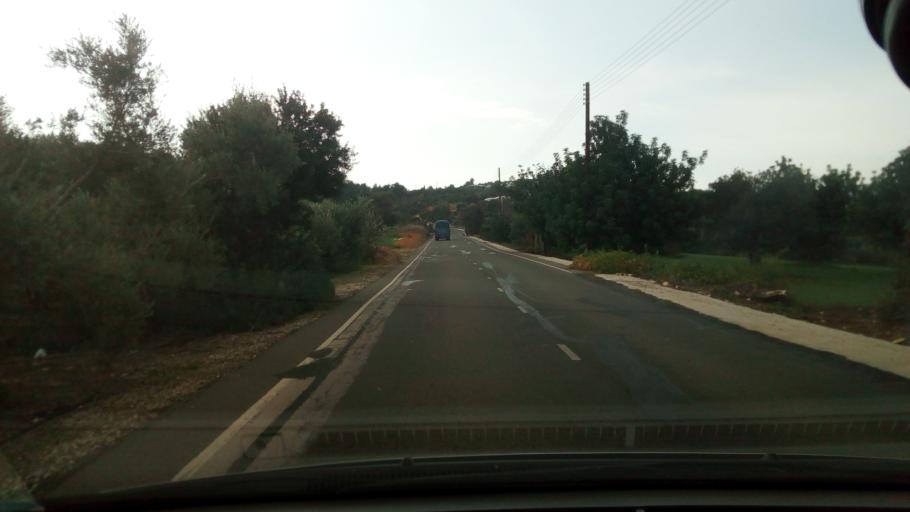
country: CY
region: Pafos
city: Polis
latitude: 35.0365
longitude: 32.3736
